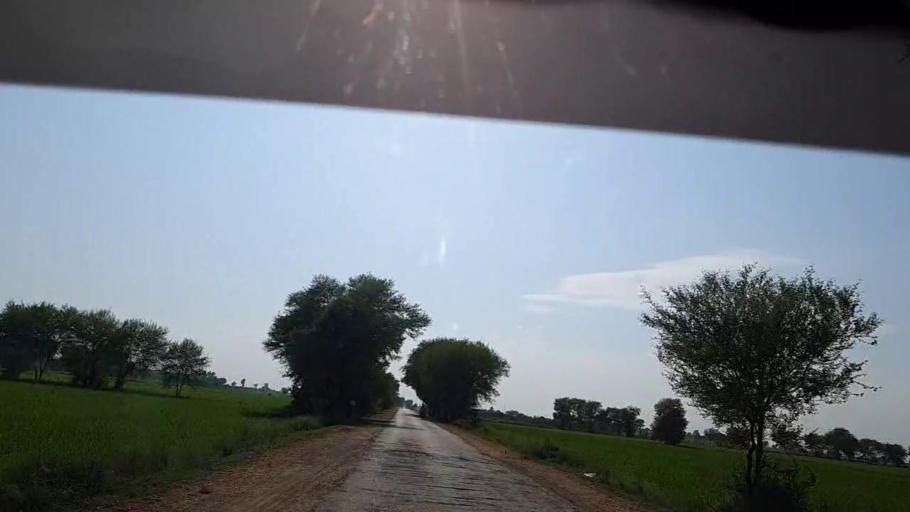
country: PK
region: Sindh
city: Shikarpur
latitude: 28.0814
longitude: 68.6495
